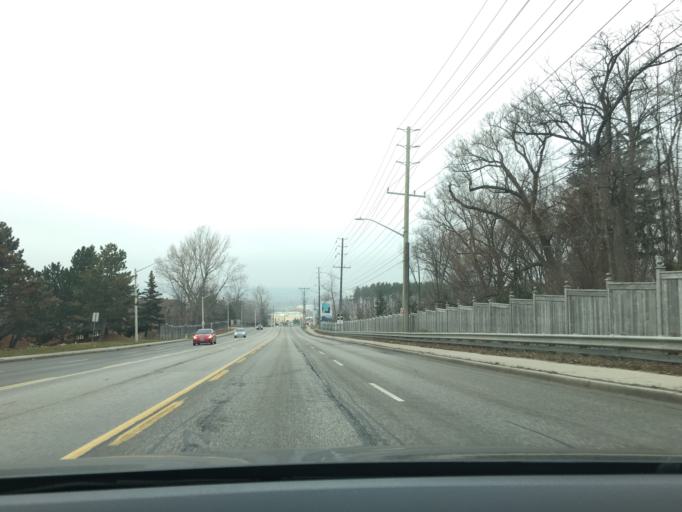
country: CA
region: Ontario
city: Barrie
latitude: 44.3530
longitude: -79.6996
